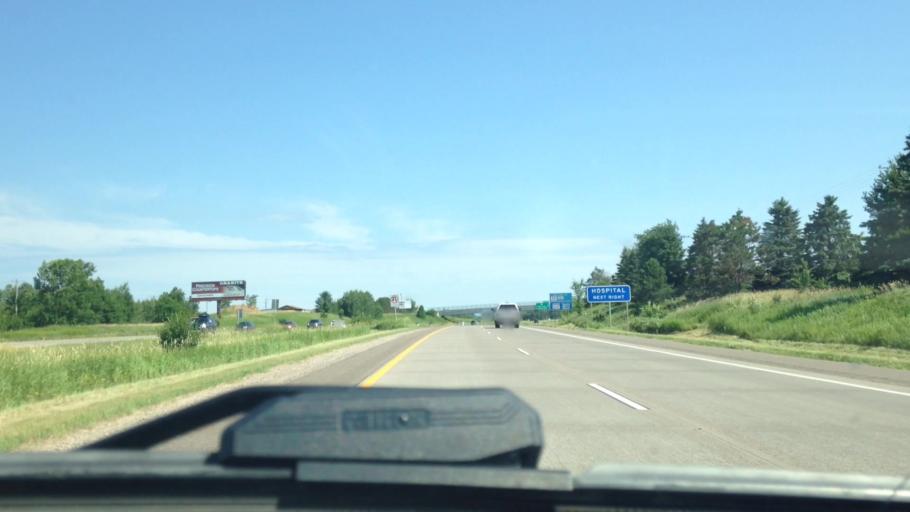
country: US
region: Wisconsin
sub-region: Barron County
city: Rice Lake
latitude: 45.4976
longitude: -91.7642
